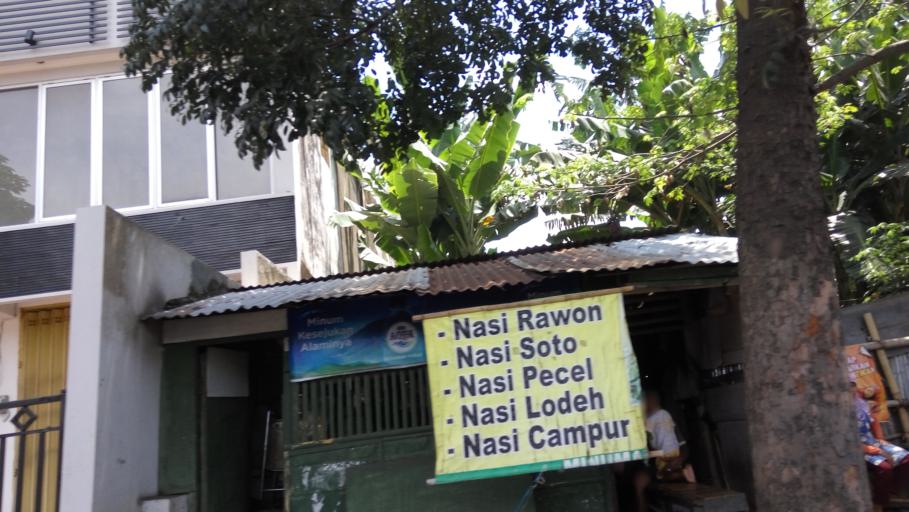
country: ID
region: East Java
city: Malang
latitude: -7.9550
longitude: 112.6385
